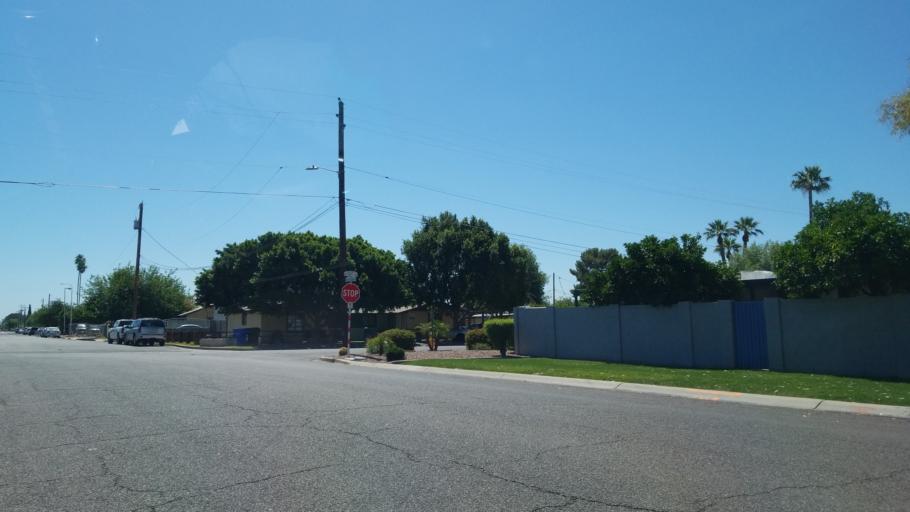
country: US
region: Arizona
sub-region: Maricopa County
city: Phoenix
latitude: 33.5058
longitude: -112.0873
